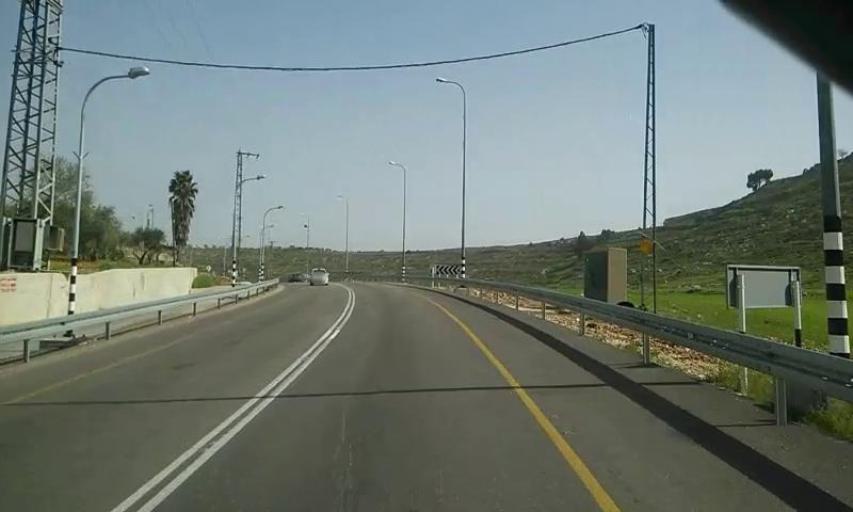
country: PS
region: West Bank
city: Sinjil
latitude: 32.0282
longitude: 35.2730
